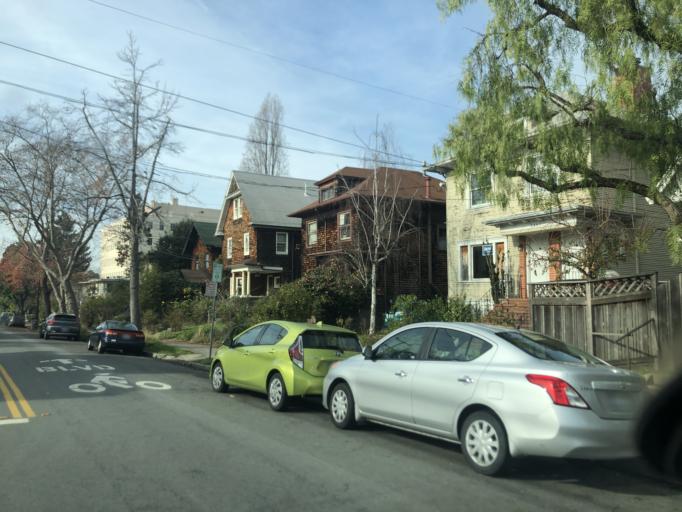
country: US
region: California
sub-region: Alameda County
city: Berkeley
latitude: 37.8580
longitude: -122.2570
